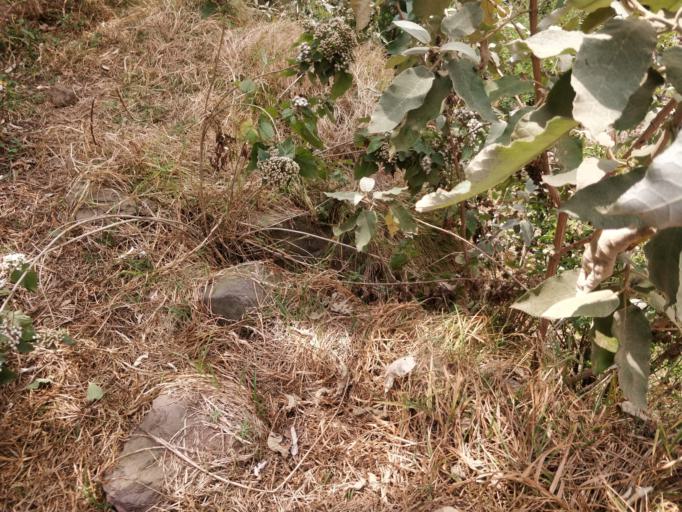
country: MX
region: Mexico City
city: Xochimilco
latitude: 19.2377
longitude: -99.0859
